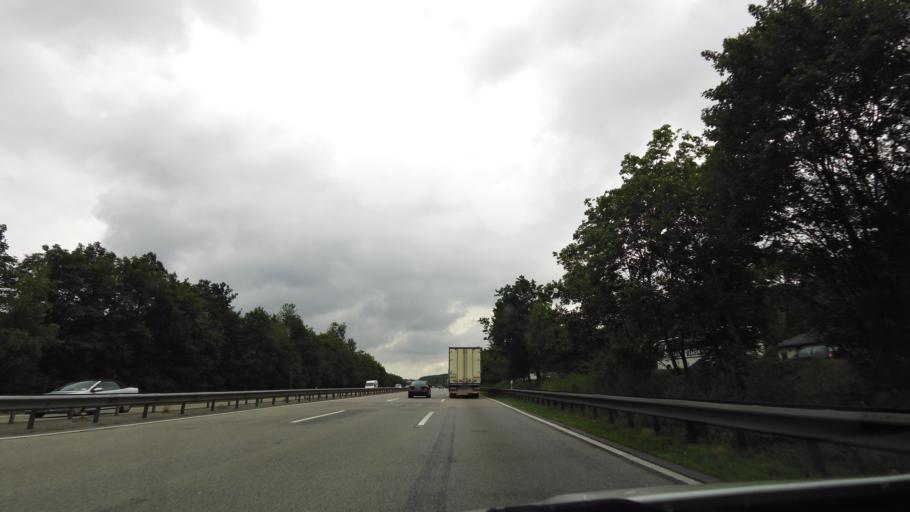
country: DE
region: Rheinland-Pfalz
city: Konigsfeld
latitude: 50.5159
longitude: 7.2015
